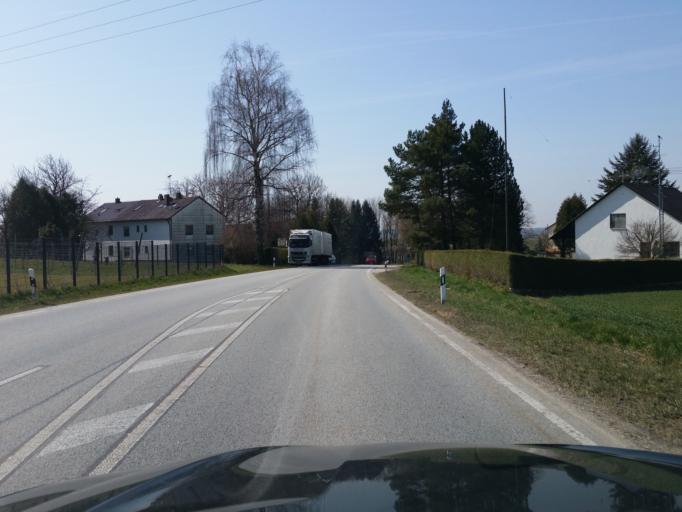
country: DE
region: Bavaria
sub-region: Lower Bavaria
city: Altfraunhofen
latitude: 48.4713
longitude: 12.1569
